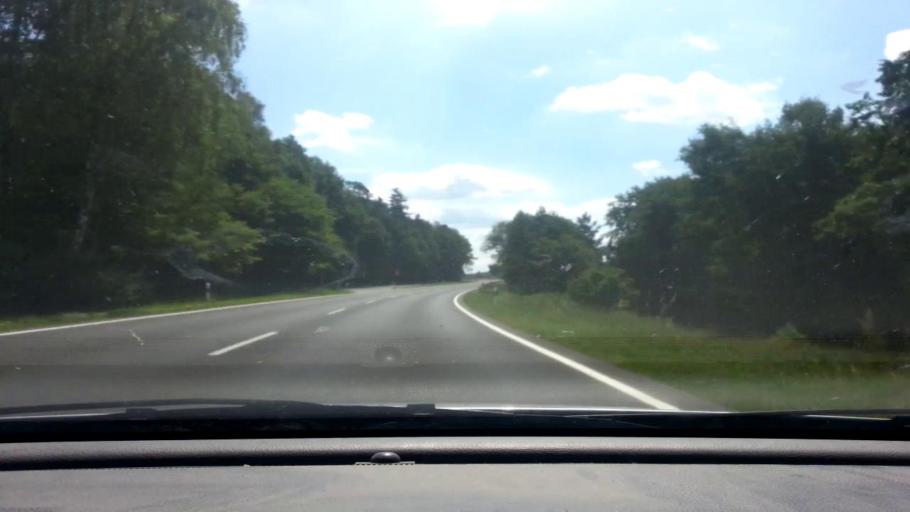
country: DE
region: Bavaria
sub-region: Upper Palatinate
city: Kastl
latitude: 49.8564
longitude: 11.9683
